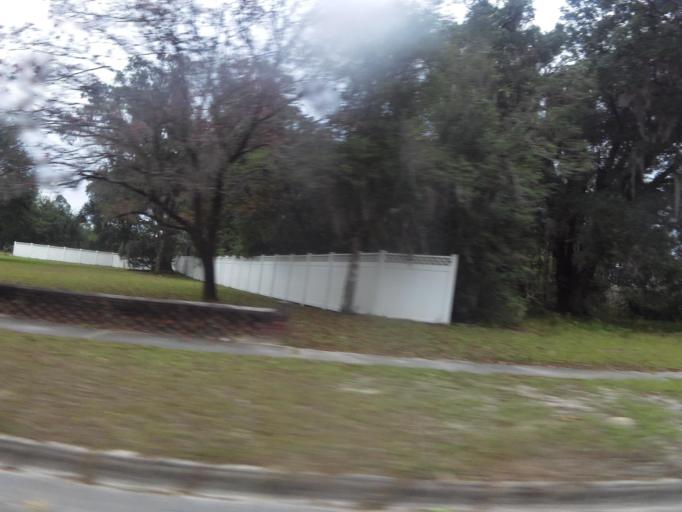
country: US
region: Georgia
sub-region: Charlton County
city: Folkston
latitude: 30.8254
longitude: -82.0096
